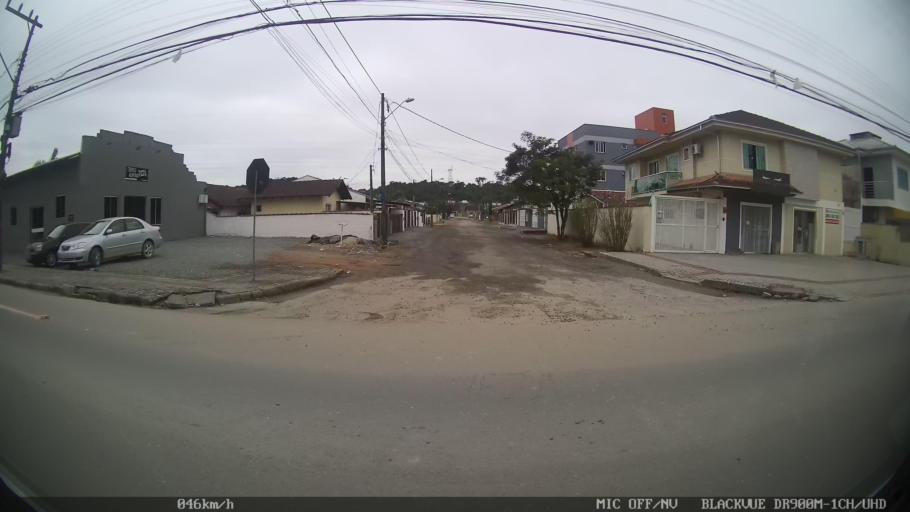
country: BR
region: Santa Catarina
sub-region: Joinville
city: Joinville
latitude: -26.2798
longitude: -48.8989
